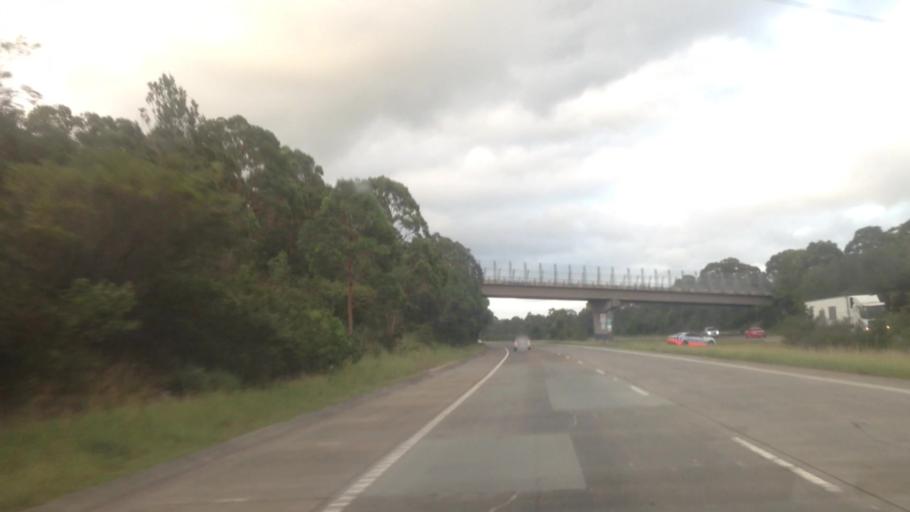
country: AU
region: New South Wales
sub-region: Wyong Shire
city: Charmhaven
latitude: -33.1949
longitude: 151.4654
